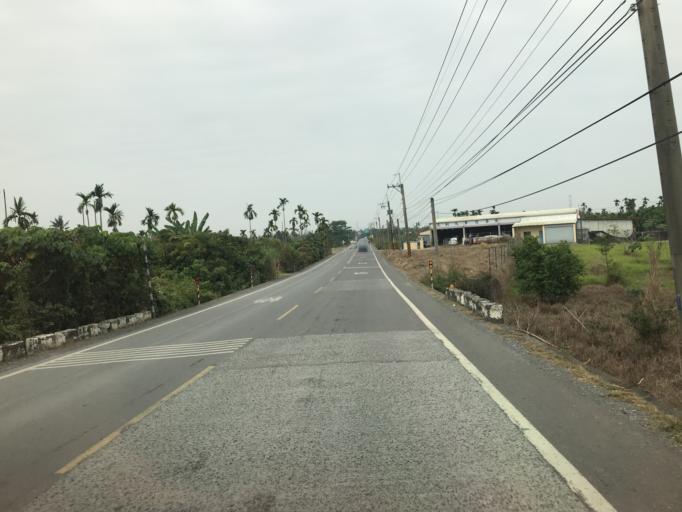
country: TW
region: Taiwan
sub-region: Pingtung
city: Pingtung
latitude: 22.4688
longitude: 120.6091
